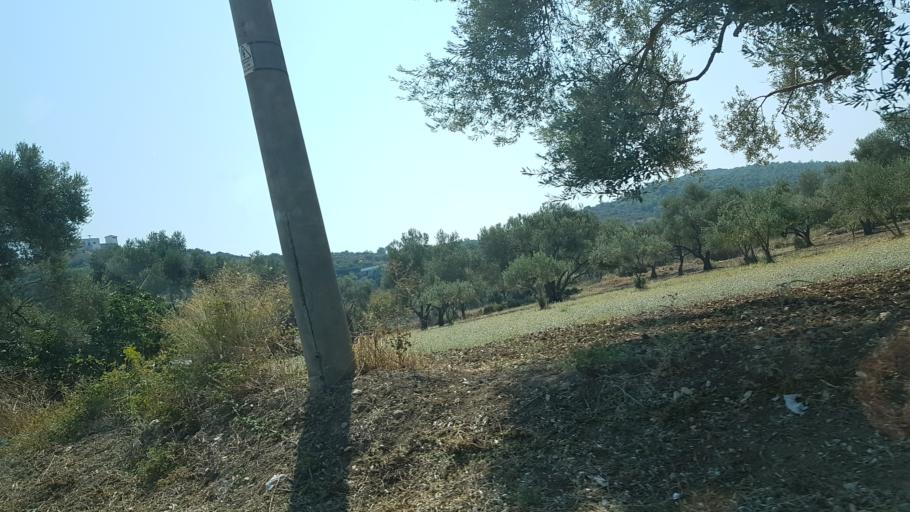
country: TR
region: Izmir
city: Urla
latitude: 38.3798
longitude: 26.7509
